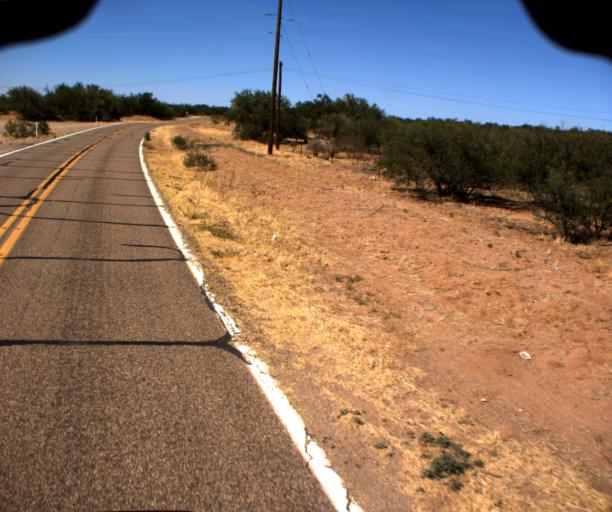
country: US
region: Arizona
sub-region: Pima County
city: Three Points
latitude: 31.8825
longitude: -111.3962
